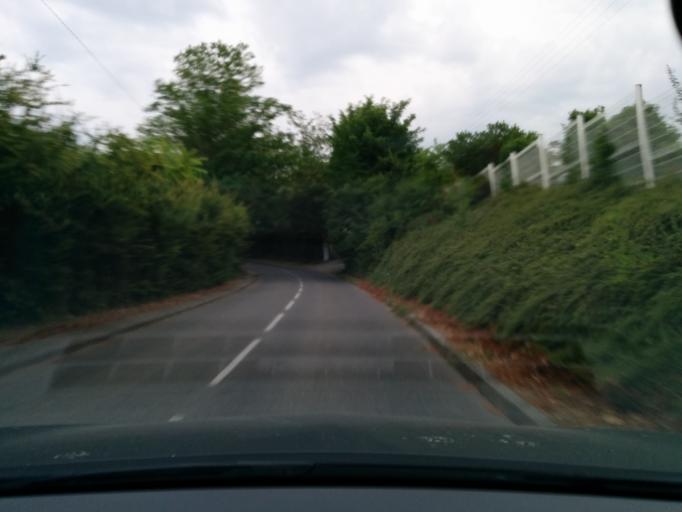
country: FR
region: Midi-Pyrenees
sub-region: Departement de la Haute-Garonne
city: Castanet-Tolosan
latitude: 43.5127
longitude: 1.4908
